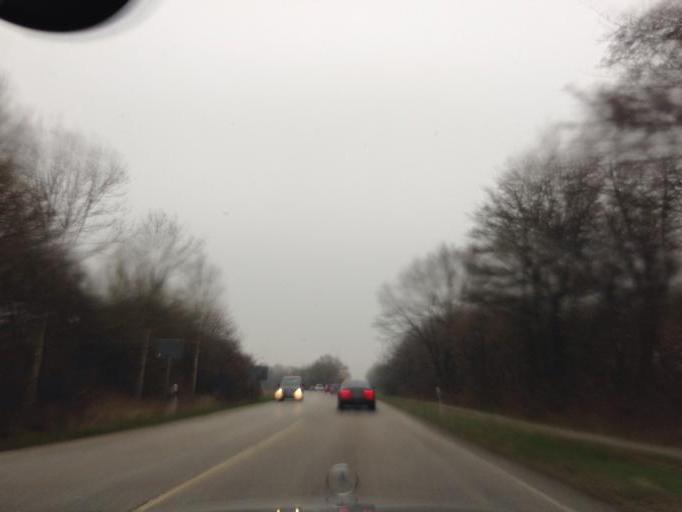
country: DE
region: Schleswig-Holstein
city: Warnau
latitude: 54.1854
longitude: 10.1717
